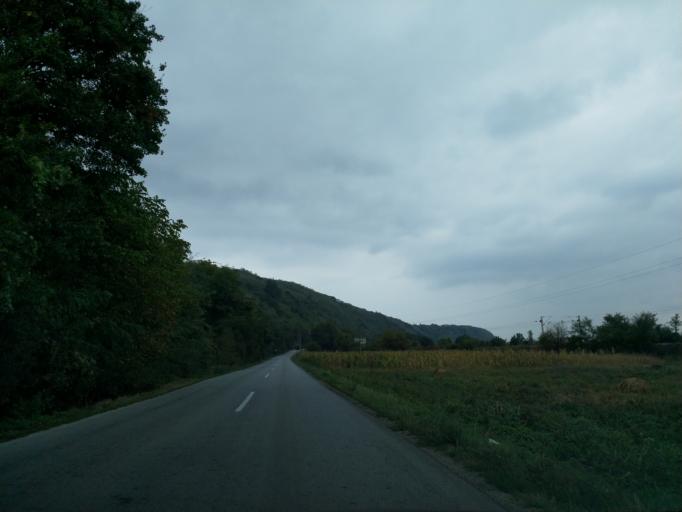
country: RS
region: Central Serbia
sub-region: Sumadijski Okrug
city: Batocina
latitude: 44.0880
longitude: 21.1702
